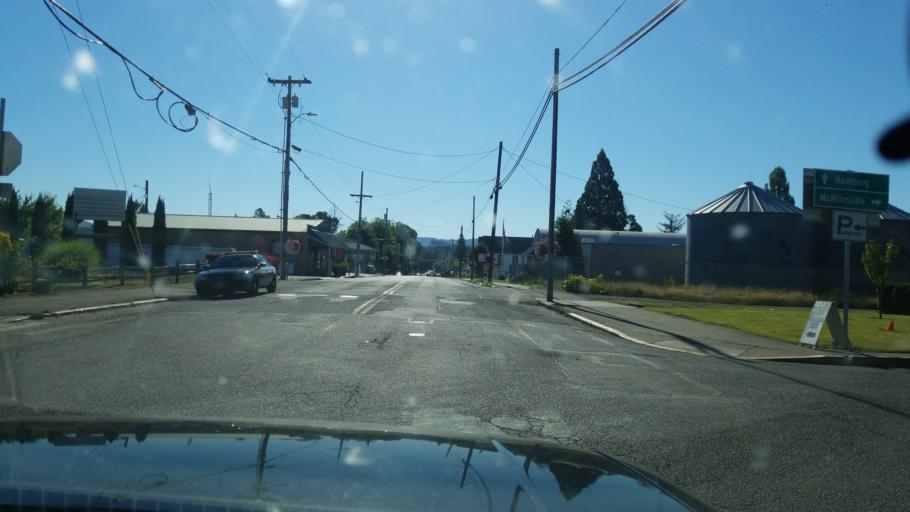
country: US
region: Oregon
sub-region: Yamhill County
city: Carlton
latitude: 45.2942
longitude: -123.1771
